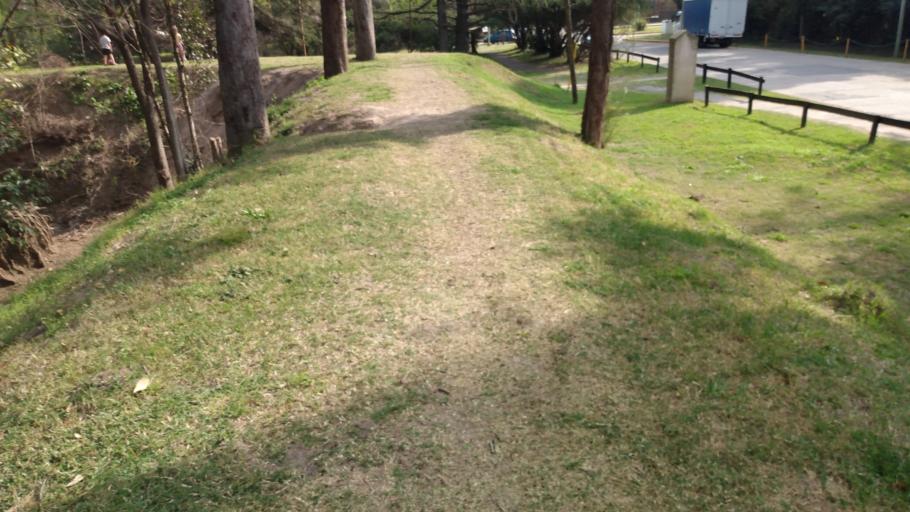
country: AR
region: Buenos Aires
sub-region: Partido de Lujan
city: Lujan
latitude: -34.5897
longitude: -59.1832
